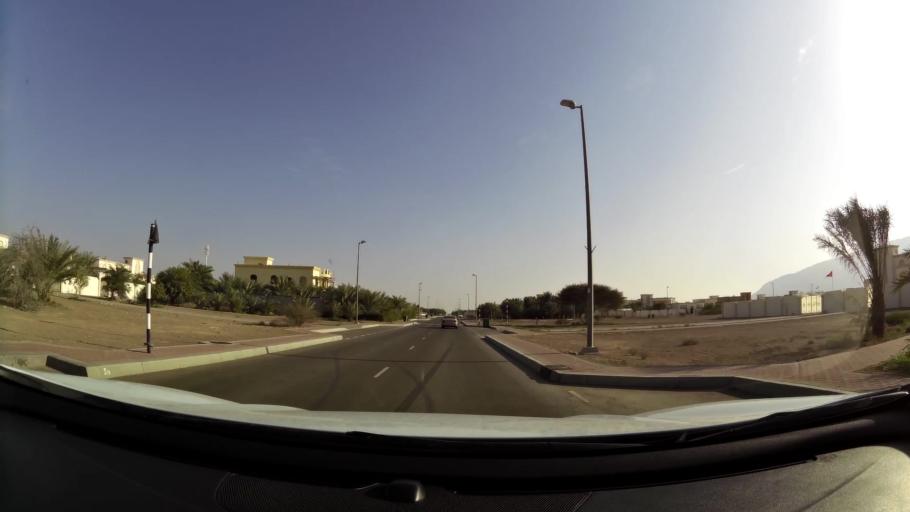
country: AE
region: Abu Dhabi
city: Al Ain
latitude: 24.0635
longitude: 55.8469
